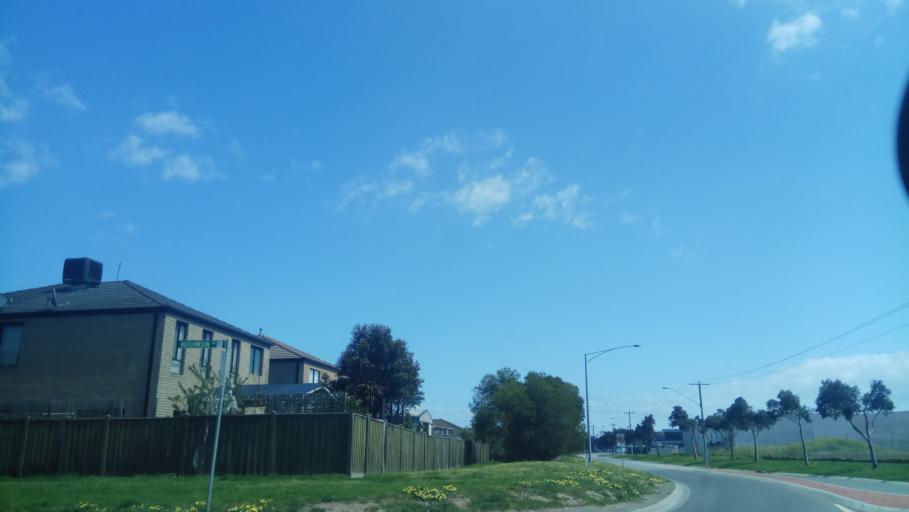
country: AU
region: Victoria
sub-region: Casey
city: Lynbrook
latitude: -38.0460
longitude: 145.2507
